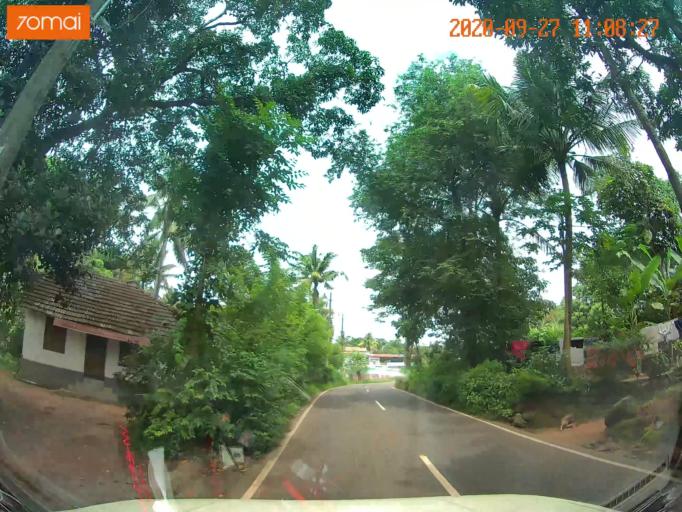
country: IN
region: Kerala
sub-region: Thrissur District
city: Trichur
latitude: 10.4304
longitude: 76.2329
